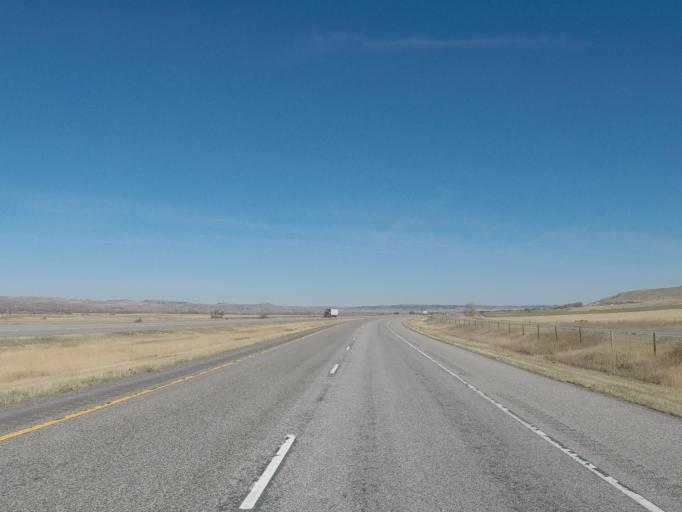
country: US
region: Montana
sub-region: Sweet Grass County
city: Big Timber
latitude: 45.8046
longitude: -110.0212
